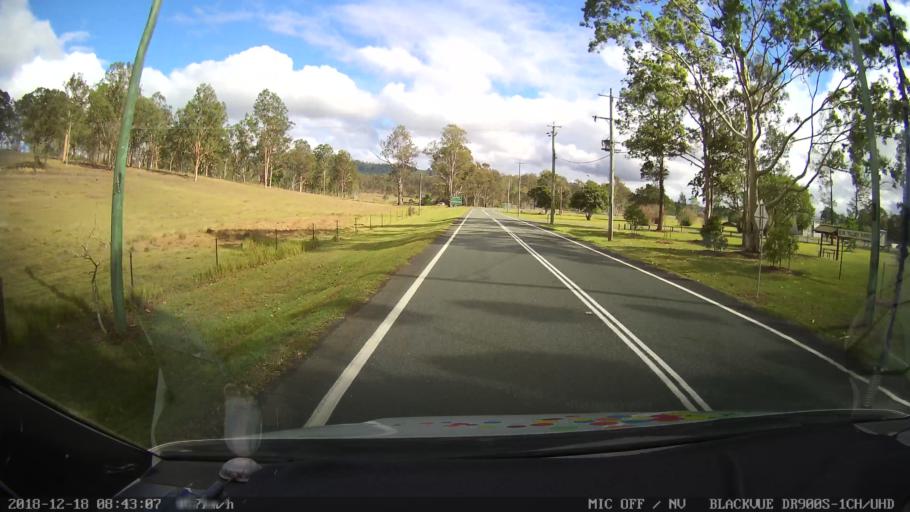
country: AU
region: Queensland
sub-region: Logan
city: Cedar Vale
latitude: -28.2211
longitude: 152.8584
